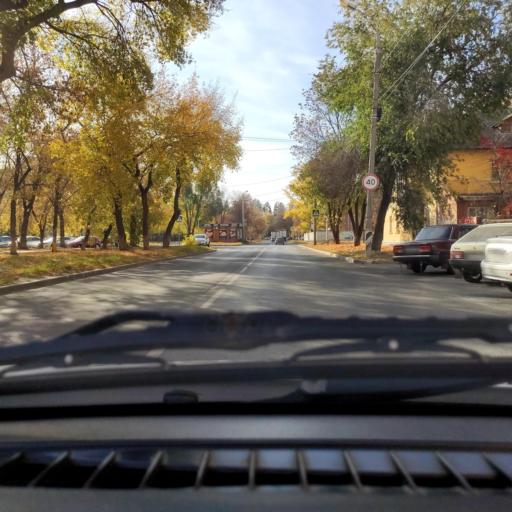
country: RU
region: Samara
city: Tol'yatti
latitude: 53.5018
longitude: 49.3966
